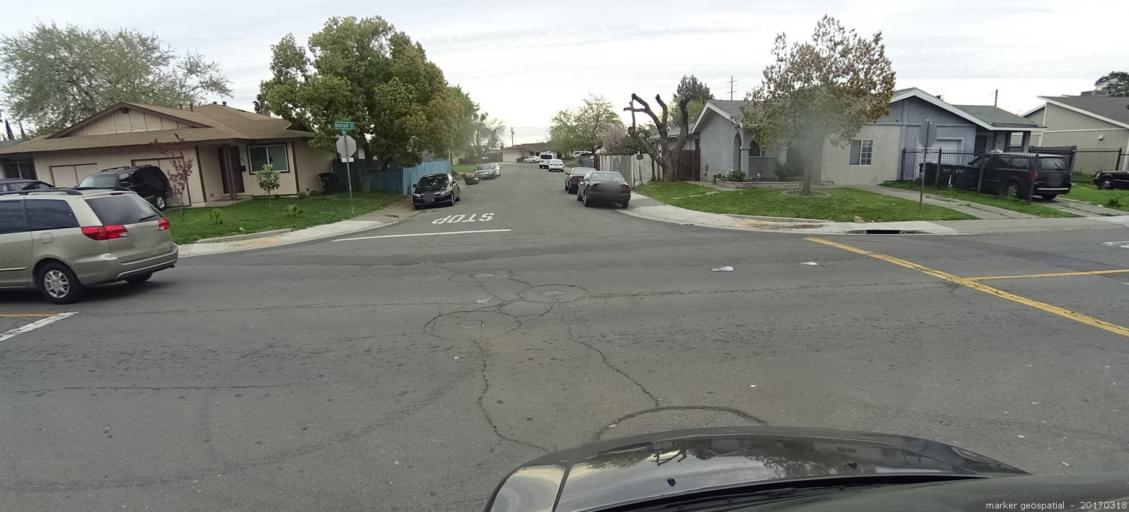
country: US
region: California
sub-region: Sacramento County
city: Parkway
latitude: 38.4725
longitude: -121.4667
